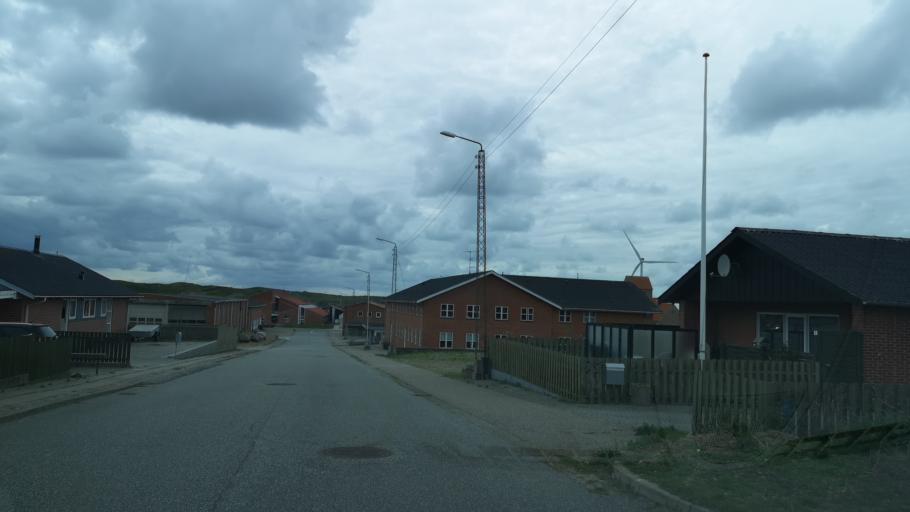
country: DK
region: Central Jutland
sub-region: Ringkobing-Skjern Kommune
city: Hvide Sande
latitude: 55.9975
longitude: 8.1302
